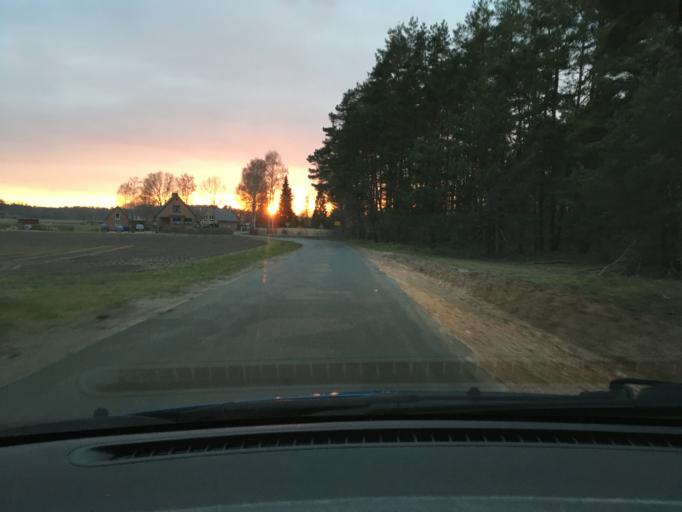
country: DE
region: Lower Saxony
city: Bleckede
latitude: 53.2924
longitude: 10.6933
